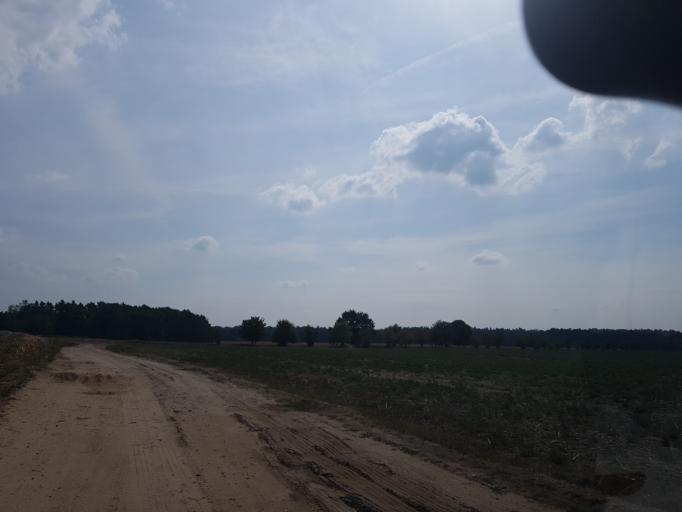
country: DE
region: Brandenburg
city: Gorzke
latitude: 52.0650
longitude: 12.3000
